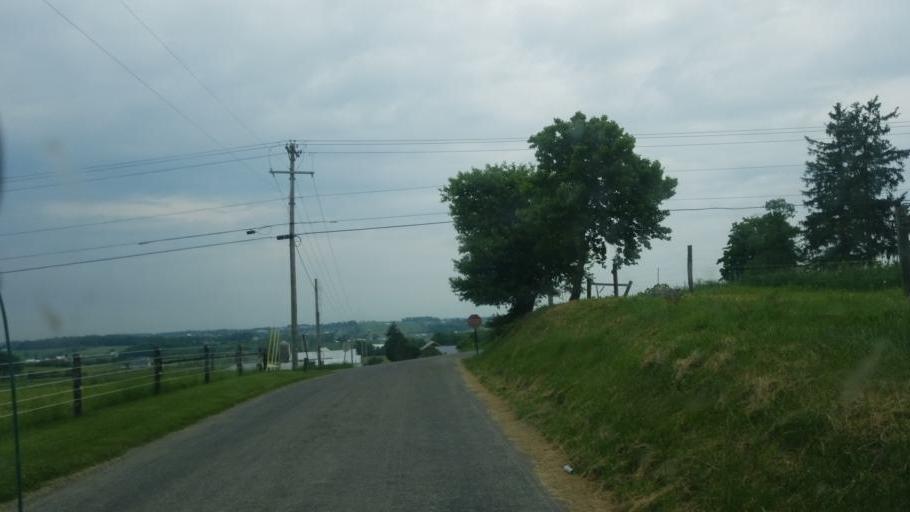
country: US
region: Ohio
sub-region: Stark County
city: Brewster
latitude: 40.6529
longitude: -81.7301
